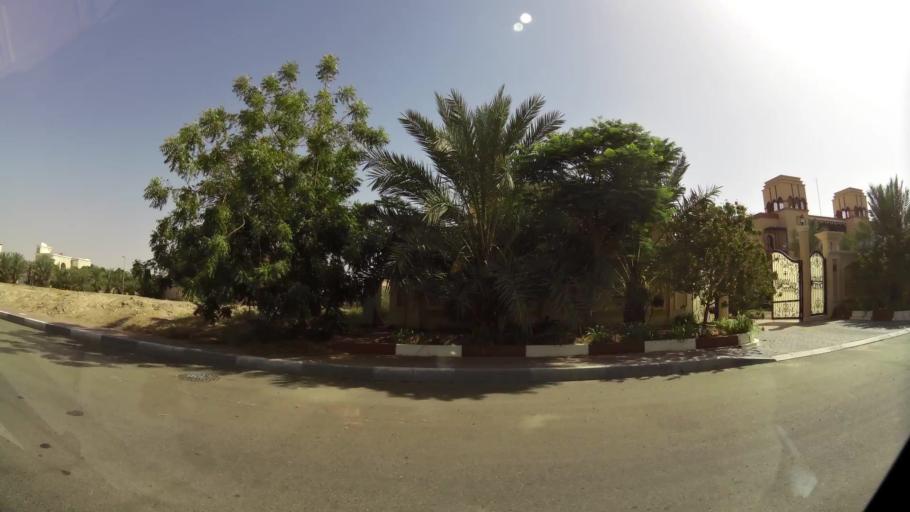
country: OM
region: Al Buraimi
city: Al Buraymi
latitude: 24.3155
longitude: 55.8043
